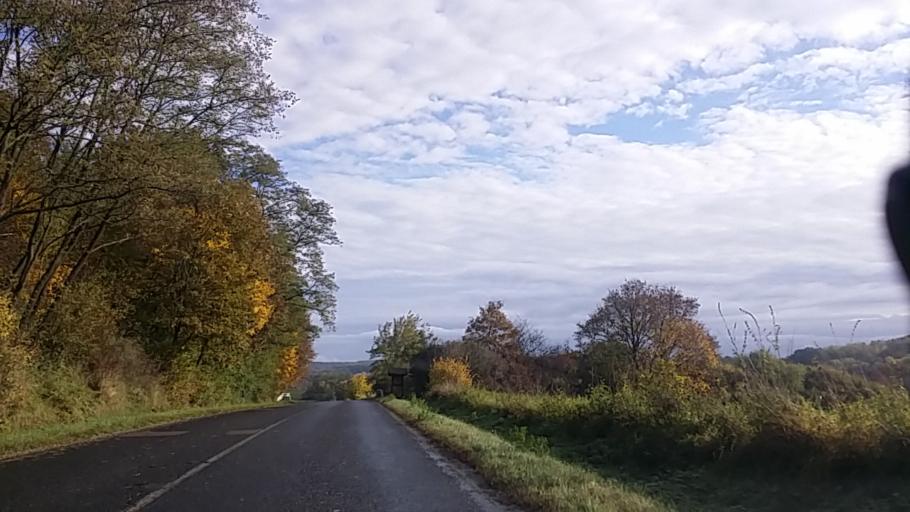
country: HU
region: Heves
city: Szilvasvarad
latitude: 48.1579
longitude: 20.4665
